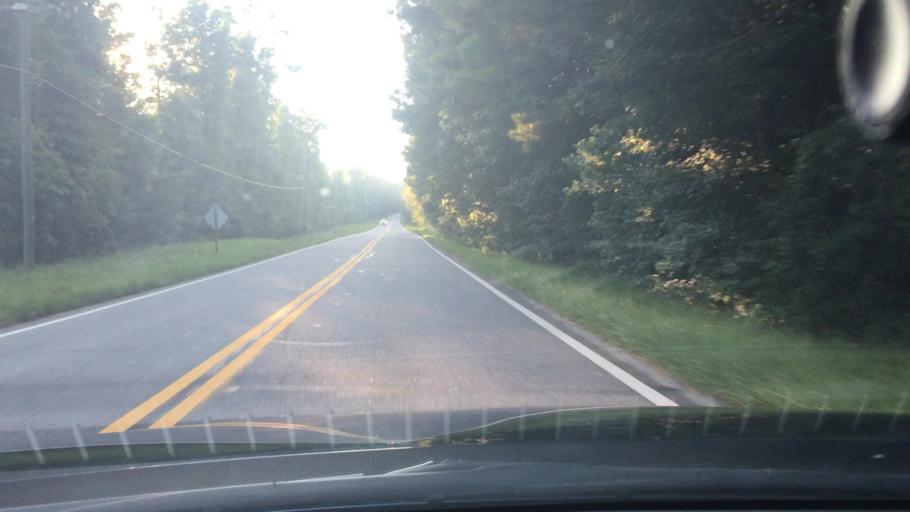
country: US
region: Georgia
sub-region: Coweta County
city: East Newnan
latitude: 33.3435
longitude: -84.7444
